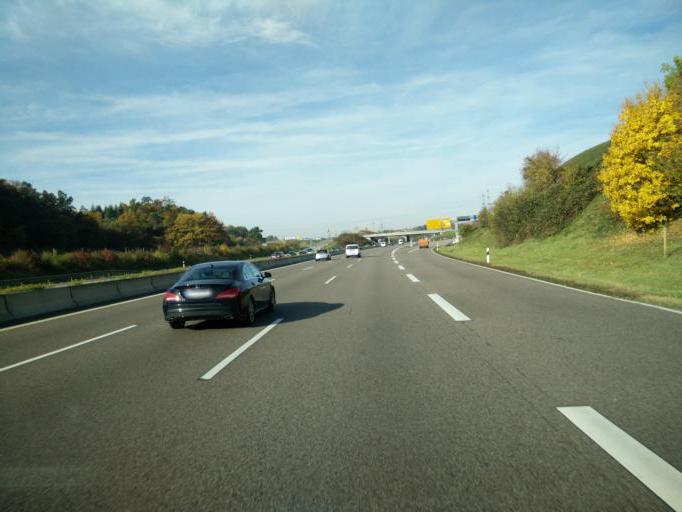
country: DE
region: Baden-Wuerttemberg
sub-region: Regierungsbezirk Stuttgart
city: Leonberg
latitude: 48.7866
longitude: 8.9865
